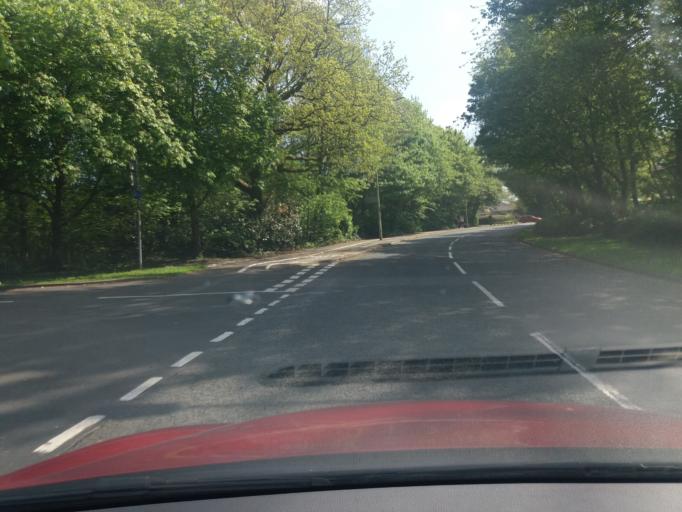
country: GB
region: England
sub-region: Lancashire
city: Chorley
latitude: 53.6663
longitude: -2.6426
